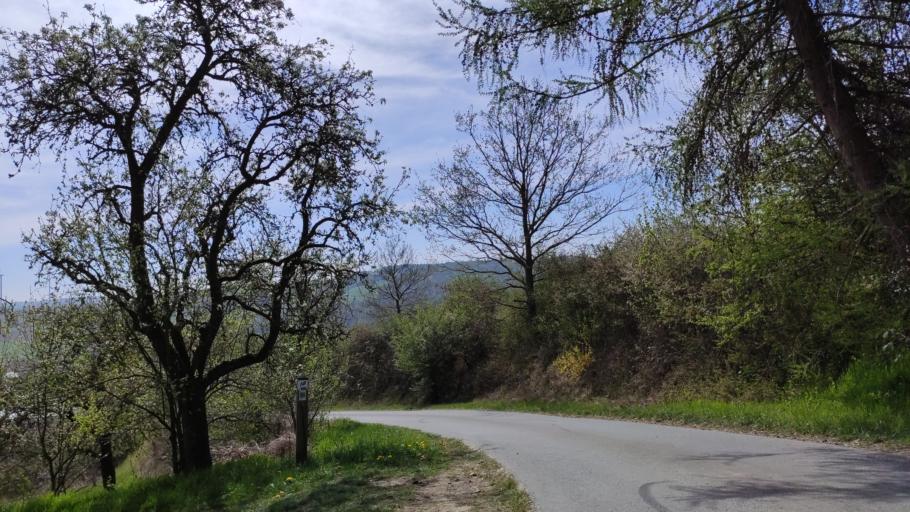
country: DE
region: North Rhine-Westphalia
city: Beverungen
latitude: 51.7146
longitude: 9.2989
